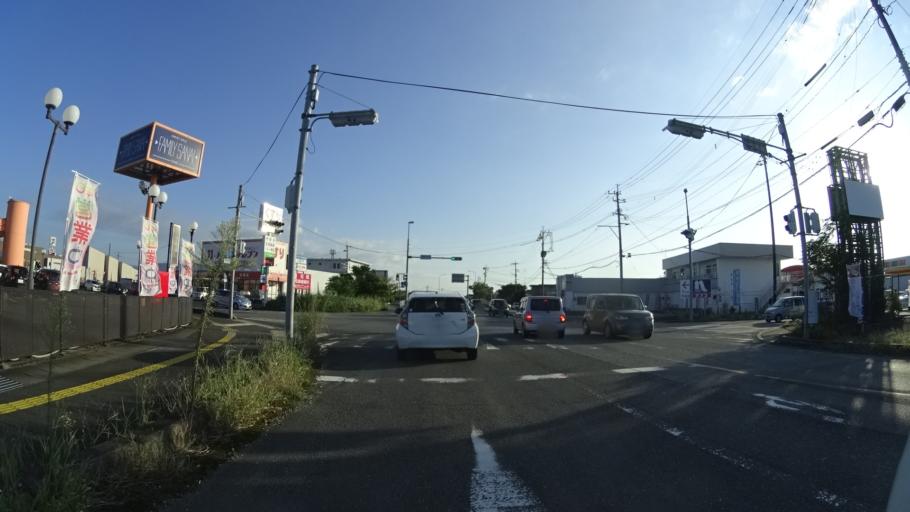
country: JP
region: Kumamoto
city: Matsubase
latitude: 32.6470
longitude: 130.6767
